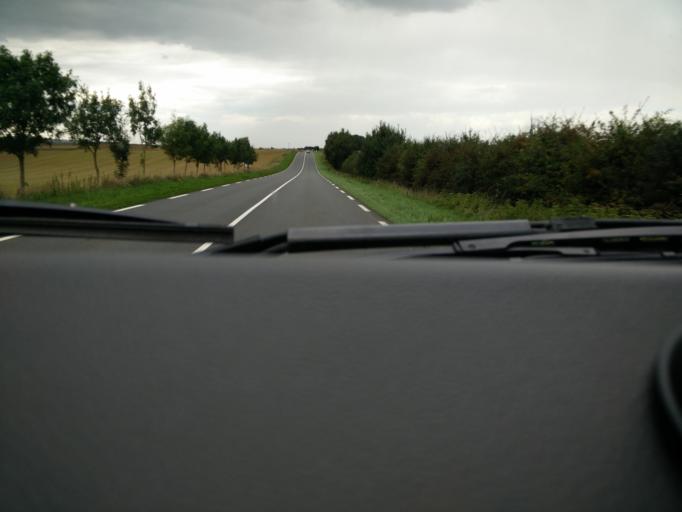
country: FR
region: Picardie
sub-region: Departement de l'Aisne
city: Saint-Michel
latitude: 49.8710
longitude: 4.1834
